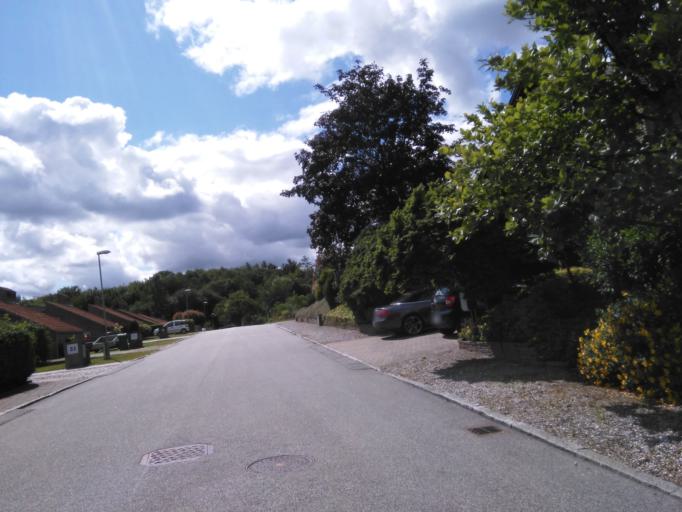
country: DK
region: Central Jutland
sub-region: Arhus Kommune
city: Arhus
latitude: 56.1108
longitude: 10.2160
